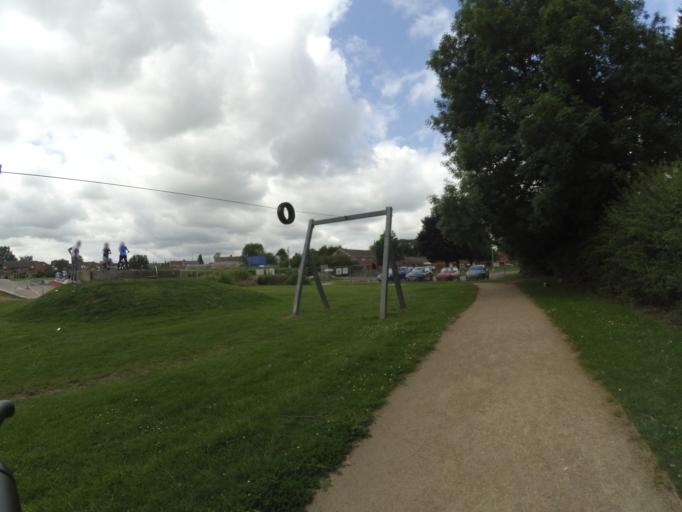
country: GB
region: England
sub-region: Warwickshire
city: Long Lawford
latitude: 52.3809
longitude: -1.3036
